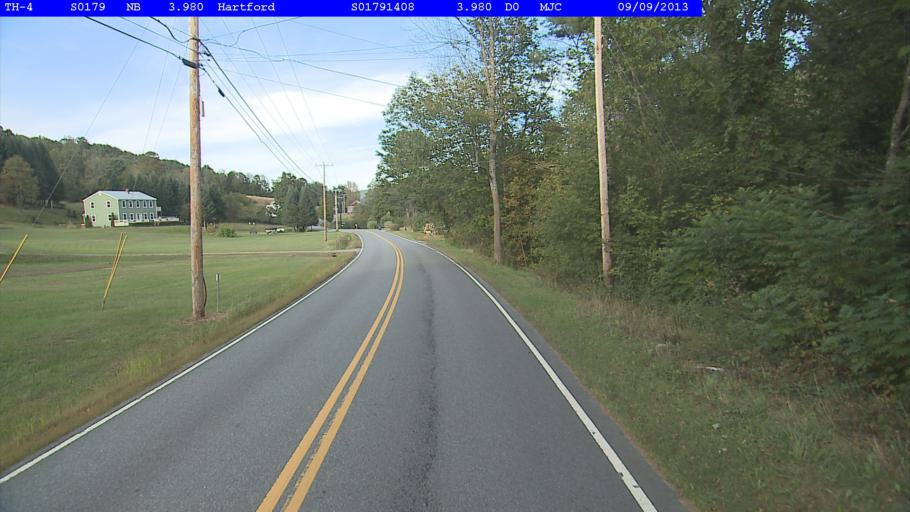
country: US
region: Vermont
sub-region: Windsor County
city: Woodstock
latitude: 43.6942
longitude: -72.4350
